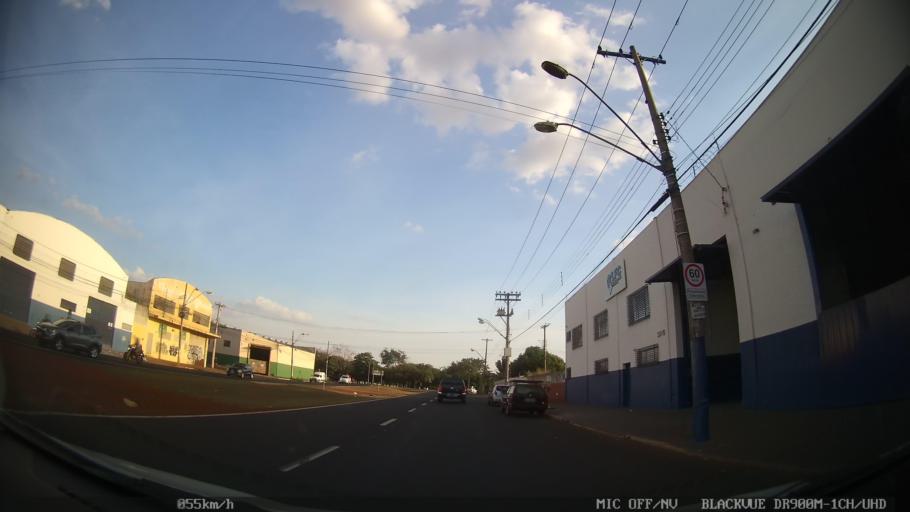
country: BR
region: Sao Paulo
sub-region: Ribeirao Preto
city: Ribeirao Preto
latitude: -21.1360
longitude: -47.7968
